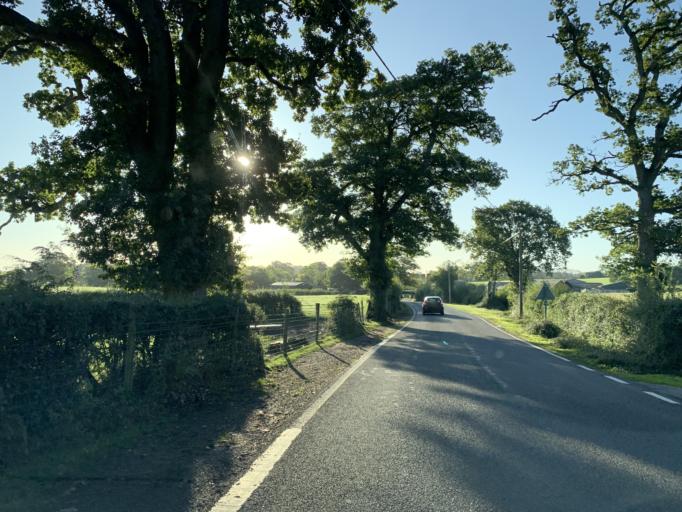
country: GB
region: England
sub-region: Hampshire
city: West Wellow
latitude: 50.9481
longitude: -1.6228
